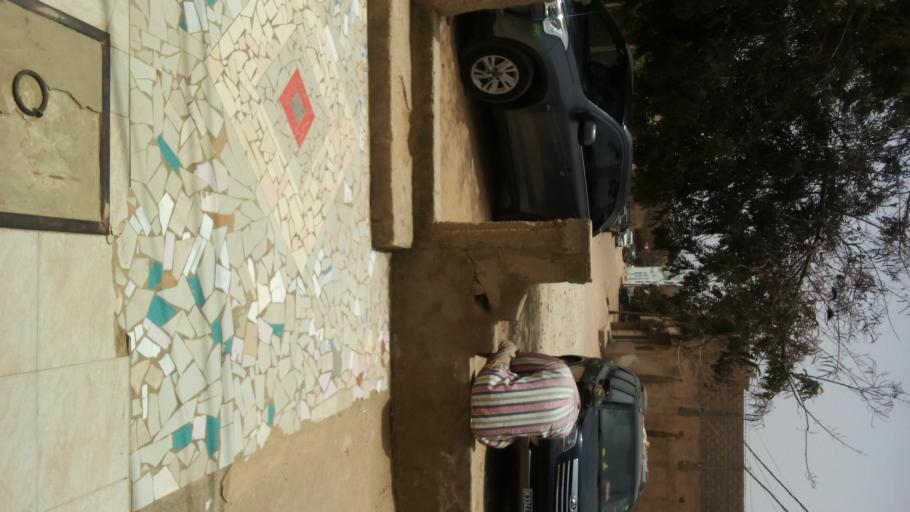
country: SN
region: Dakar
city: Pikine
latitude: 14.7241
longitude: -17.2812
